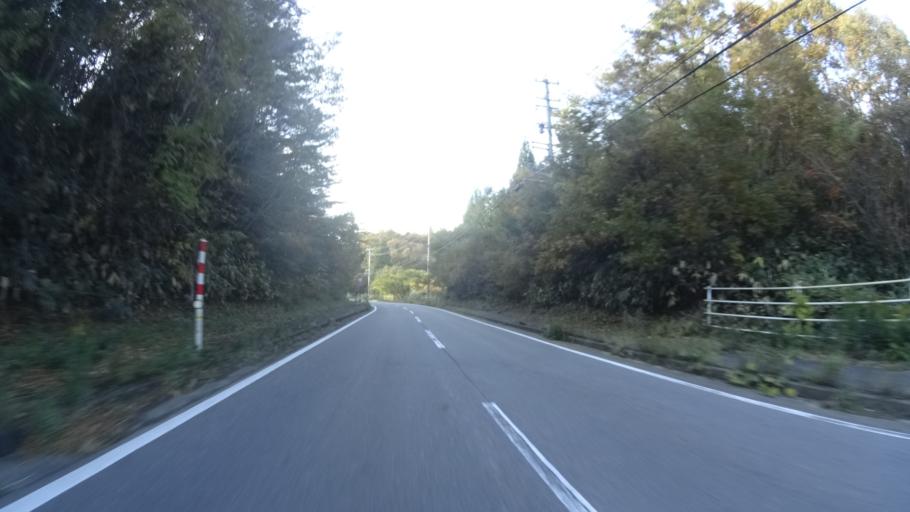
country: JP
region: Ishikawa
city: Hakui
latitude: 37.0651
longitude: 136.7716
